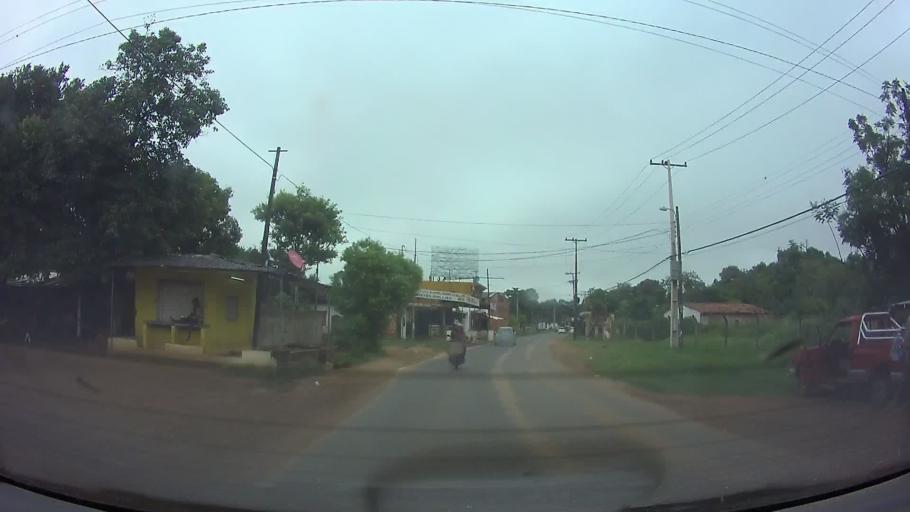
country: PY
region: Central
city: San Lorenzo
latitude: -25.3312
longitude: -57.5030
